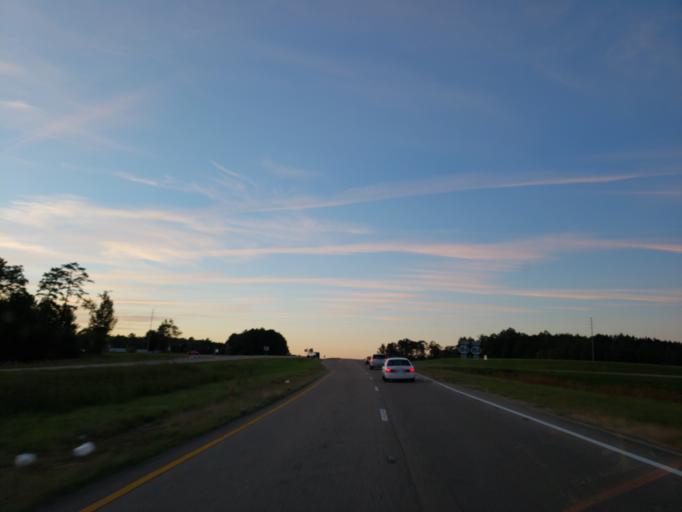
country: US
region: Mississippi
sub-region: Wayne County
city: Waynesboro
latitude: 31.6991
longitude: -88.6193
